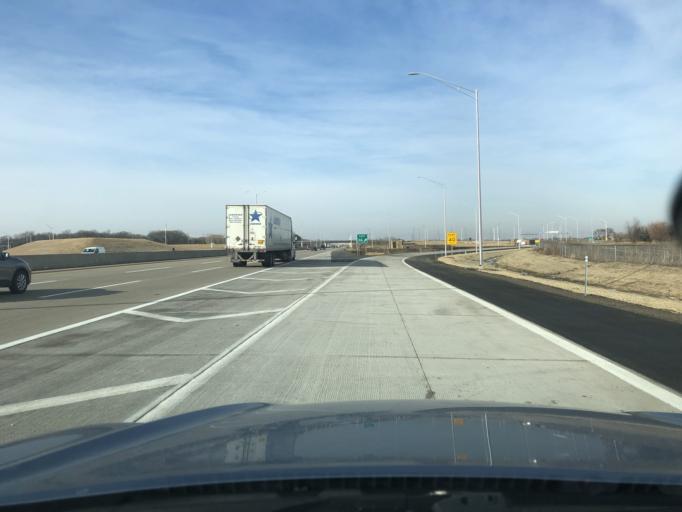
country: US
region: Illinois
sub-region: McHenry County
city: Marengo
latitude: 42.1758
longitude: -88.6101
